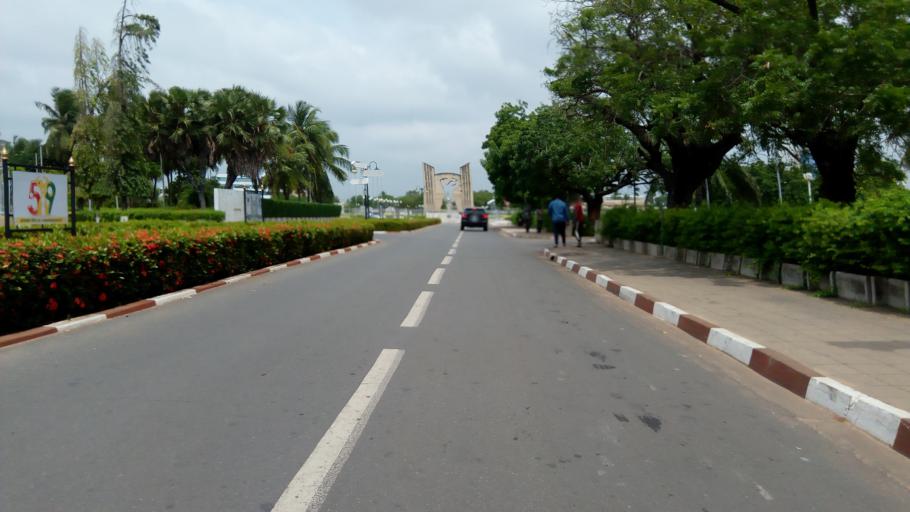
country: TG
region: Maritime
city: Lome
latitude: 6.1290
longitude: 1.2173
